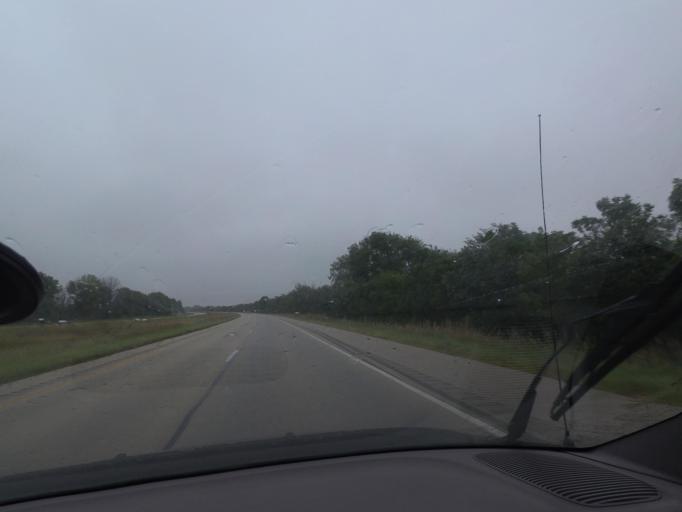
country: US
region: Illinois
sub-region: Sangamon County
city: New Berlin
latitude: 39.7412
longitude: -89.8263
